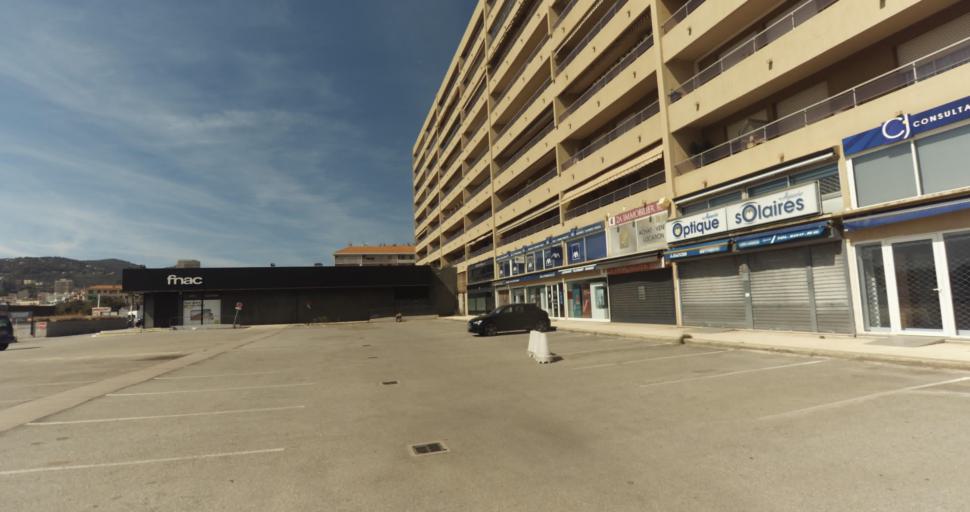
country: FR
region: Corsica
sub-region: Departement de la Corse-du-Sud
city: Ajaccio
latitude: 41.9313
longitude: 8.7454
